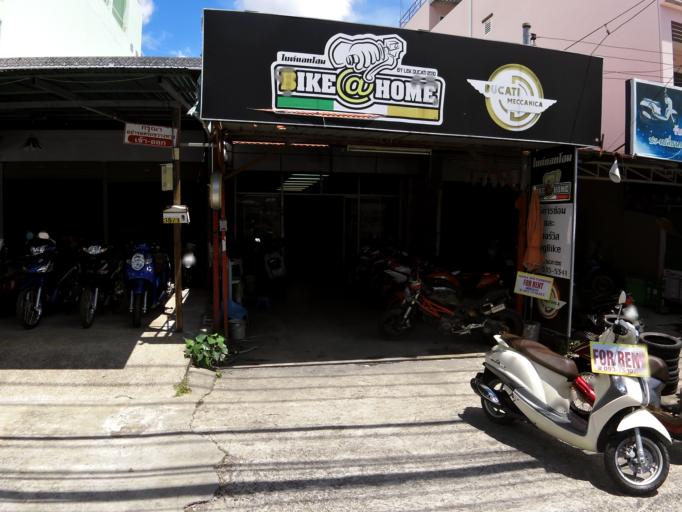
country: TH
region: Phuket
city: Ban Talat Nua
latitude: 7.8841
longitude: 98.3652
